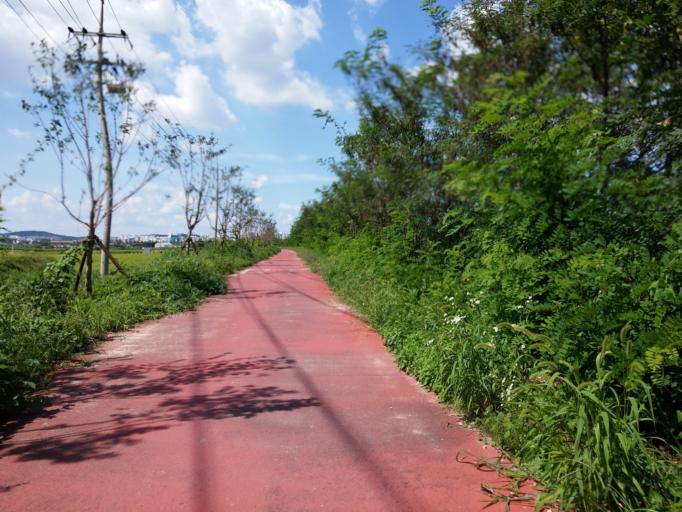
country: KR
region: Chungcheongbuk-do
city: Cheongju-si
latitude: 36.5851
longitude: 127.5009
